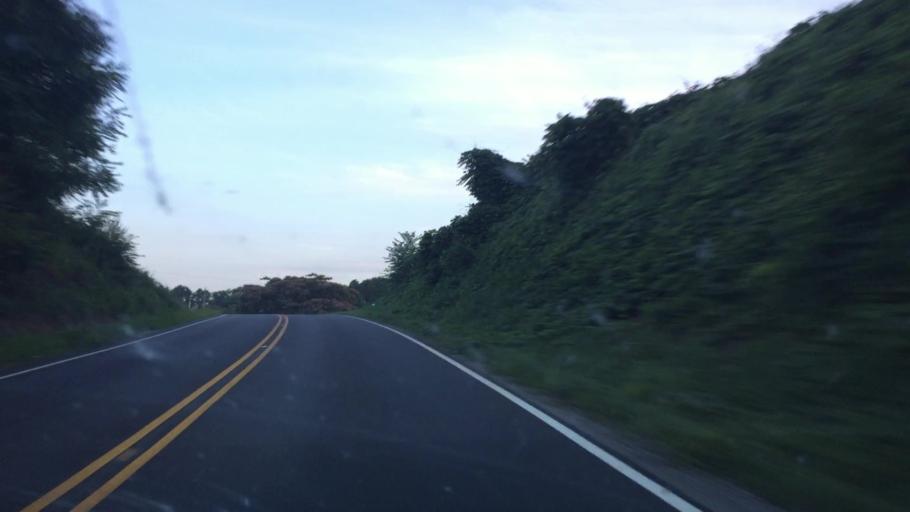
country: US
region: Virginia
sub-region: Wythe County
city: Wytheville
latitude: 36.9348
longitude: -80.9446
